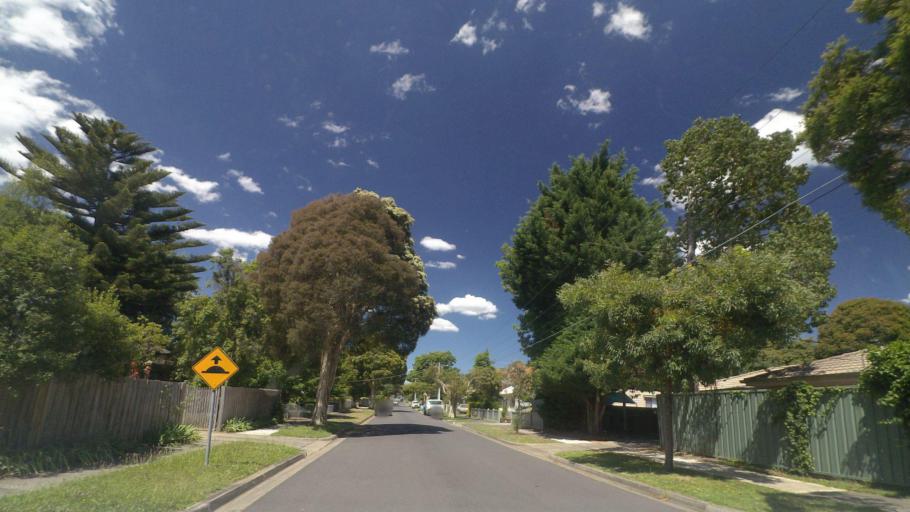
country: AU
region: Victoria
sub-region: Yarra Ranges
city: Kilsyth
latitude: -37.8066
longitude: 145.3156
